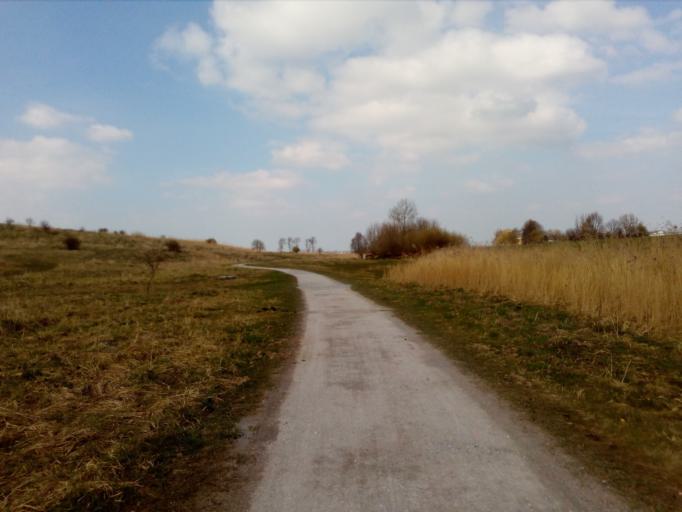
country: NL
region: South Holland
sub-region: Gemeente Zoetermeer
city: Zoetermeer
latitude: 52.0743
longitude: 4.4576
